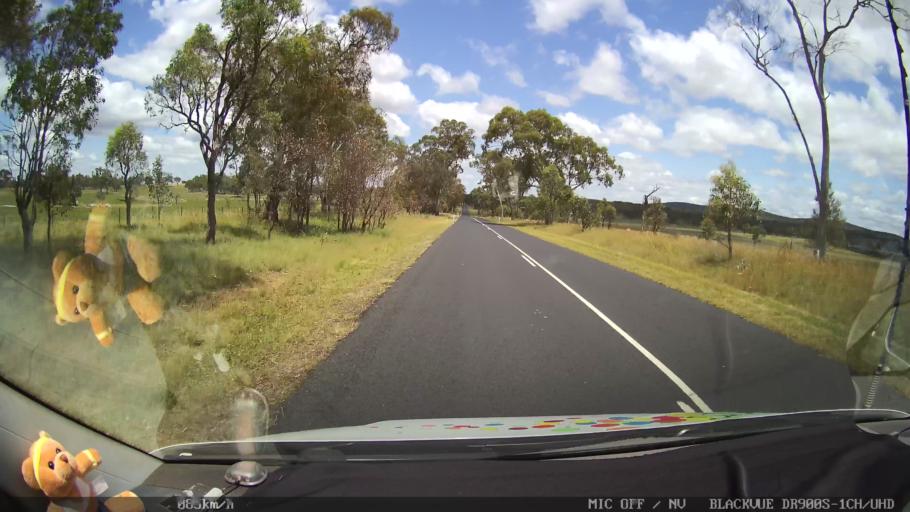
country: AU
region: New South Wales
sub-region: Glen Innes Severn
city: Glen Innes
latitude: -29.4693
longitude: 151.6552
